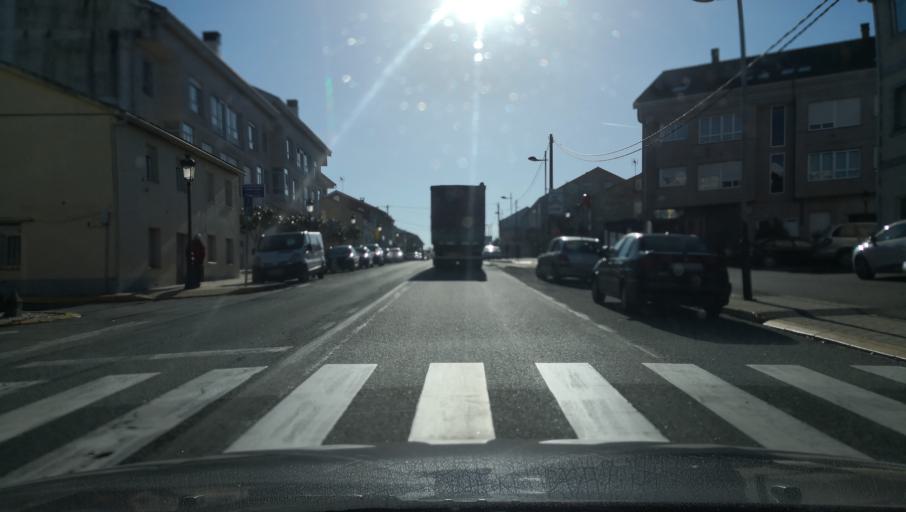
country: ES
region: Galicia
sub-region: Provincia da Coruna
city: Vedra
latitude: 42.7985
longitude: -8.4710
